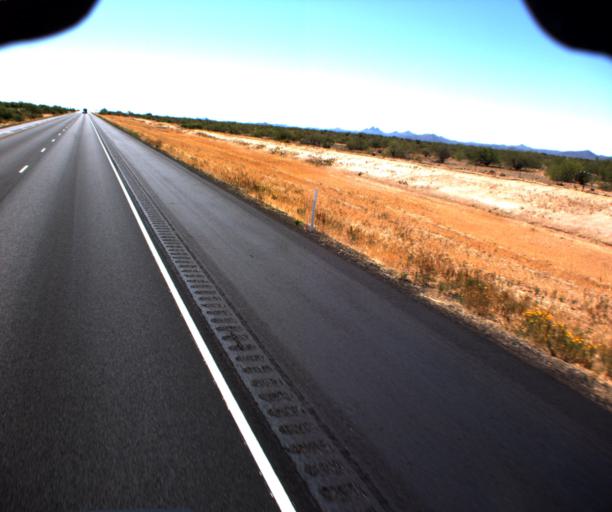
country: US
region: Arizona
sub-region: Yavapai County
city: Congress
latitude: 34.0956
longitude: -112.9112
